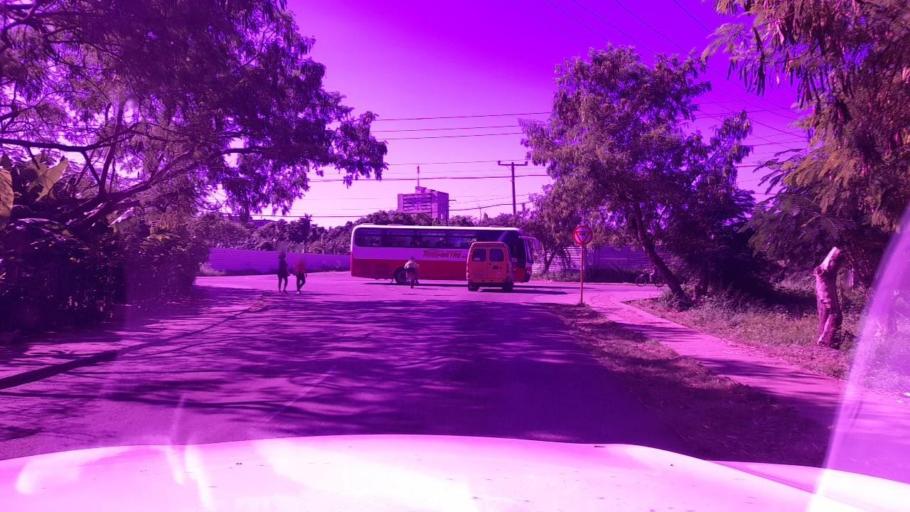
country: CU
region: La Habana
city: Alamar
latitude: 23.1658
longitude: -82.2733
